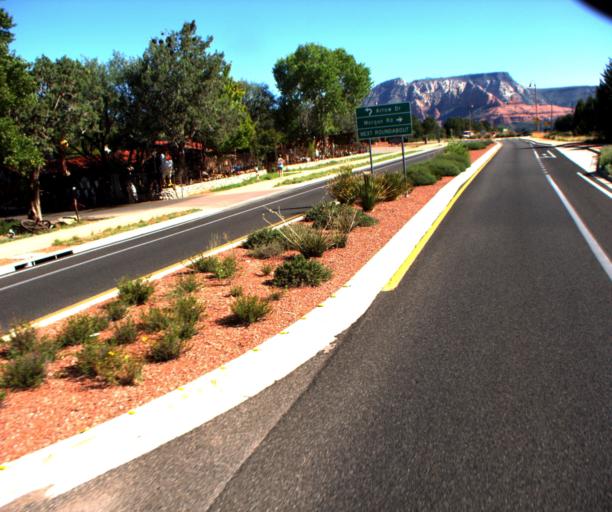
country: US
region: Arizona
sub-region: Coconino County
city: Sedona
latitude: 34.8466
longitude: -111.7666
